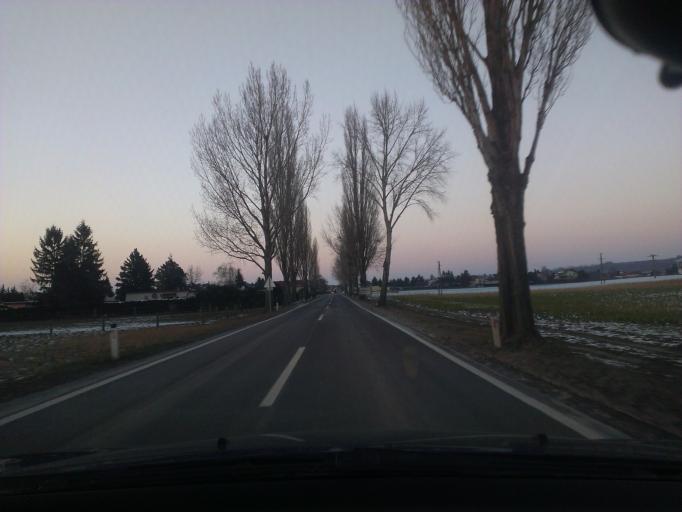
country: AT
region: Lower Austria
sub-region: Politischer Bezirk Bruck an der Leitha
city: Enzersdorf an der Fischa
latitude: 48.0737
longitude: 16.6088
